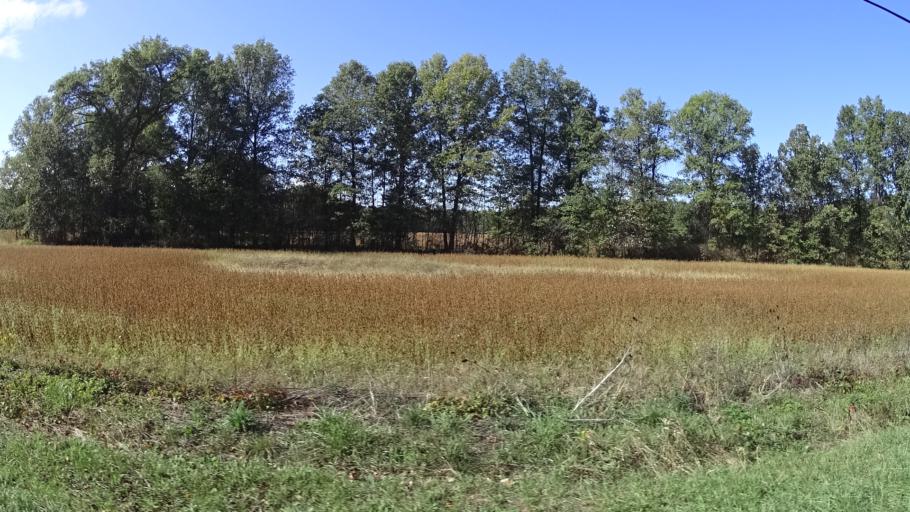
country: US
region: Ohio
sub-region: Lorain County
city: Grafton
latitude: 41.2682
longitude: -82.0796
